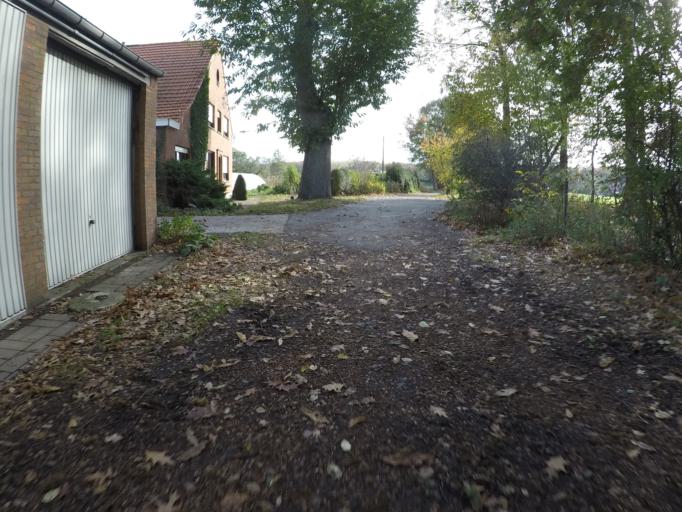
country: BE
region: Flanders
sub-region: Provincie Vlaams-Brabant
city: Begijnendijk
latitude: 51.0300
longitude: 4.7794
